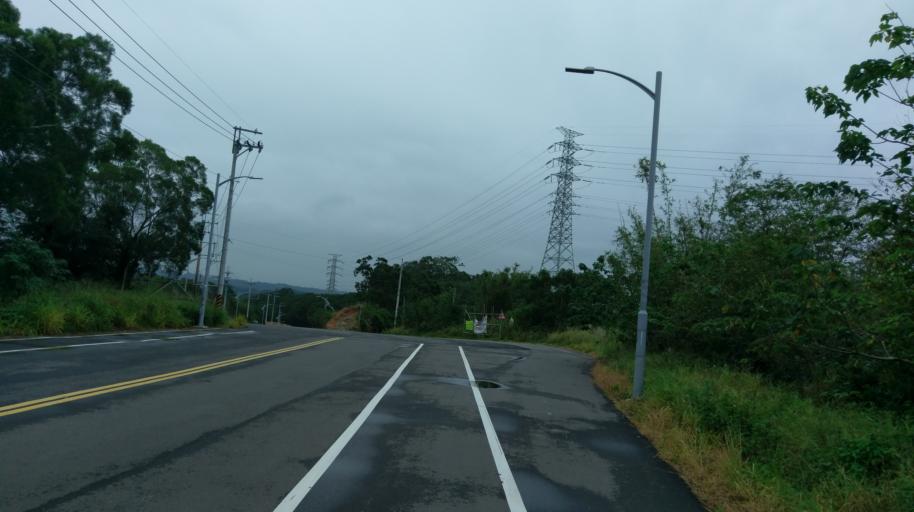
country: TW
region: Taiwan
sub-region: Hsinchu
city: Hsinchu
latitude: 24.7473
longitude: 120.9573
